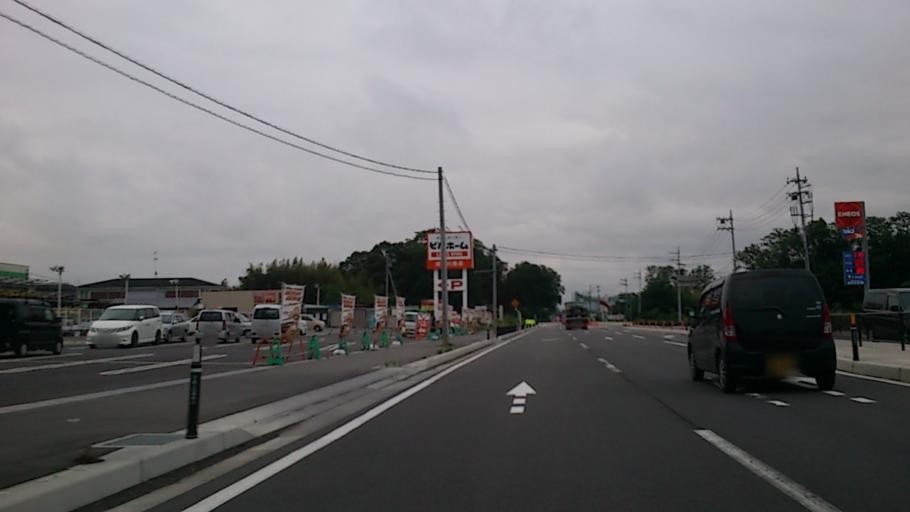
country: JP
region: Fukushima
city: Sukagawa
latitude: 37.2695
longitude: 140.3571
